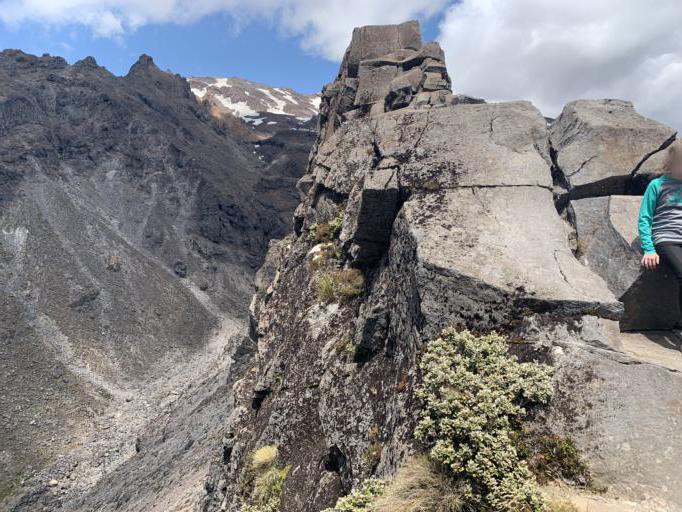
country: NZ
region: Manawatu-Wanganui
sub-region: Ruapehu District
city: Waiouru
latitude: -39.2360
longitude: 175.5614
